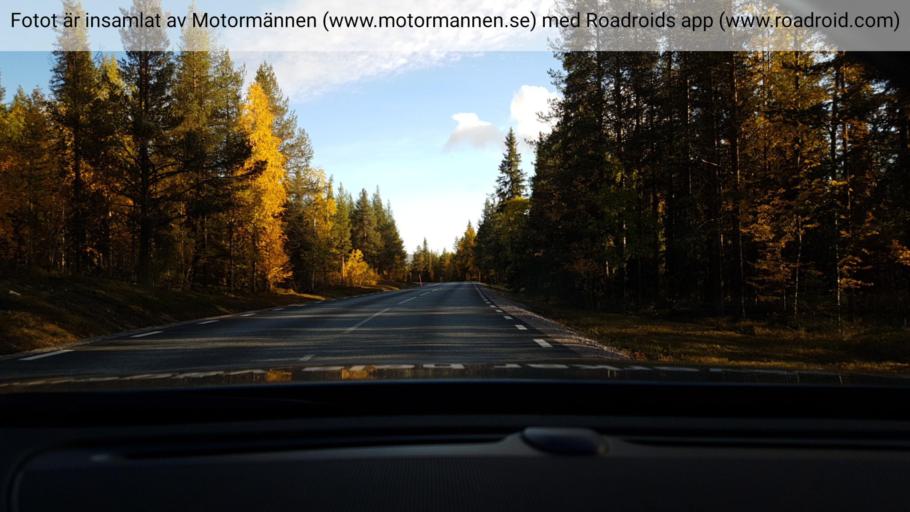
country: SE
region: Norrbotten
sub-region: Jokkmokks Kommun
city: Jokkmokk
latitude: 66.9360
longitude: 19.8178
